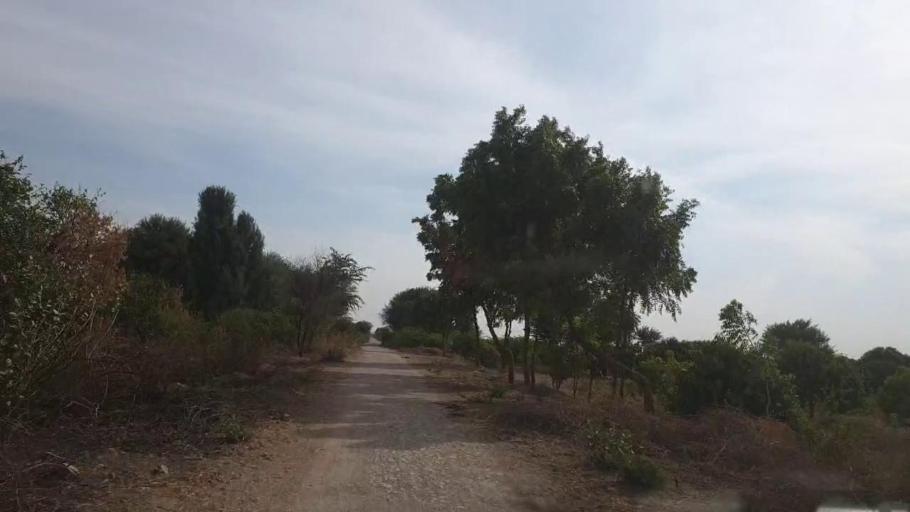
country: PK
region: Sindh
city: Nabisar
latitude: 25.0212
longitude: 69.5623
